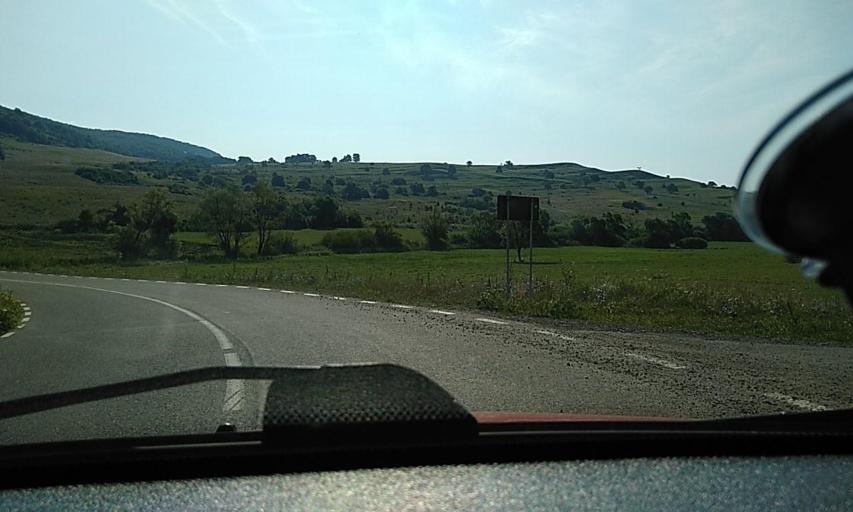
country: RO
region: Brasov
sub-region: Comuna Bunesti
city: Bunesti
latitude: 46.0825
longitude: 25.0620
